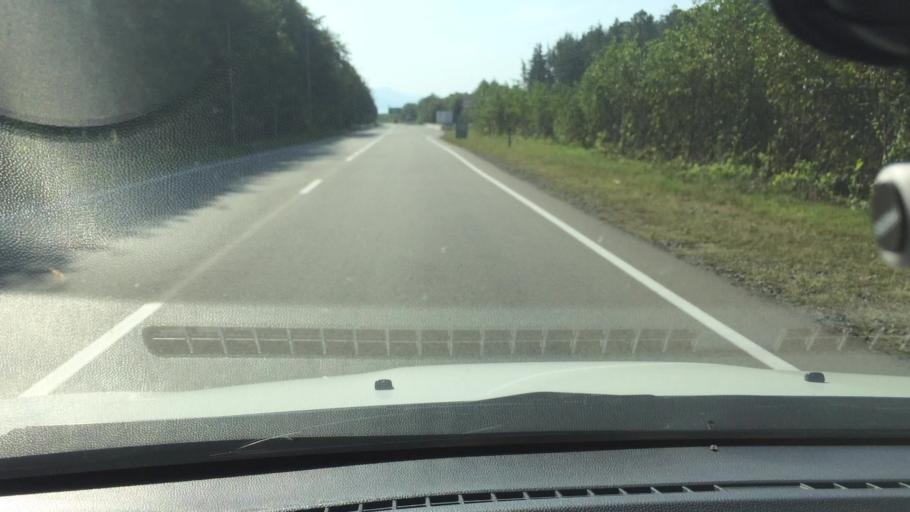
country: GE
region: Guria
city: Urek'i
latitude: 41.9454
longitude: 41.7706
